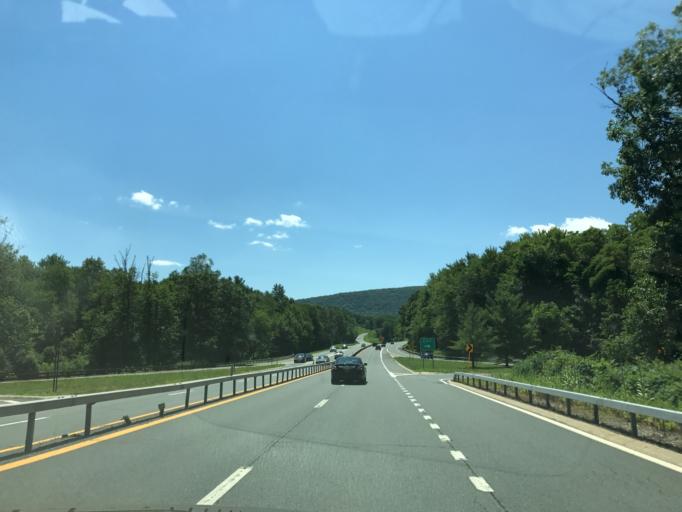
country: US
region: New York
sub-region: Dutchess County
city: Hillside Lake
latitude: 41.5573
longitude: -73.7801
